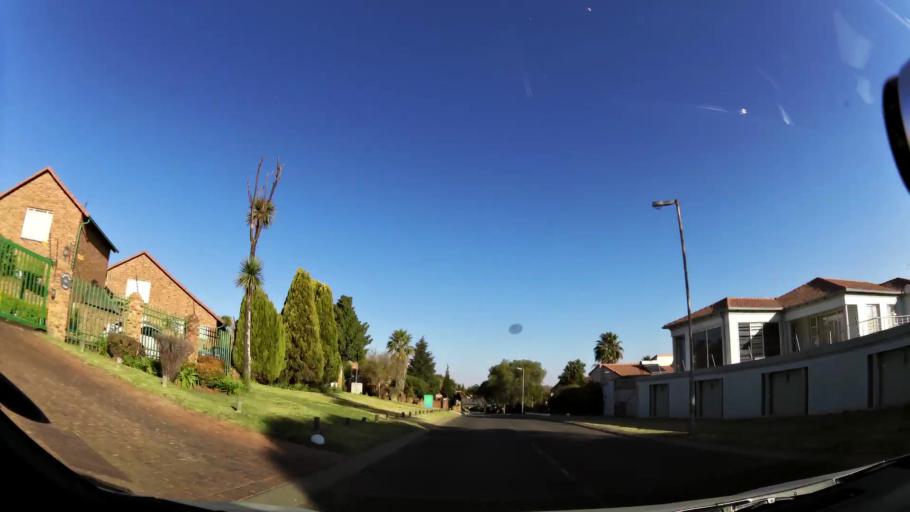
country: ZA
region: Gauteng
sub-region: City of Johannesburg Metropolitan Municipality
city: Johannesburg
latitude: -26.2821
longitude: 28.0695
